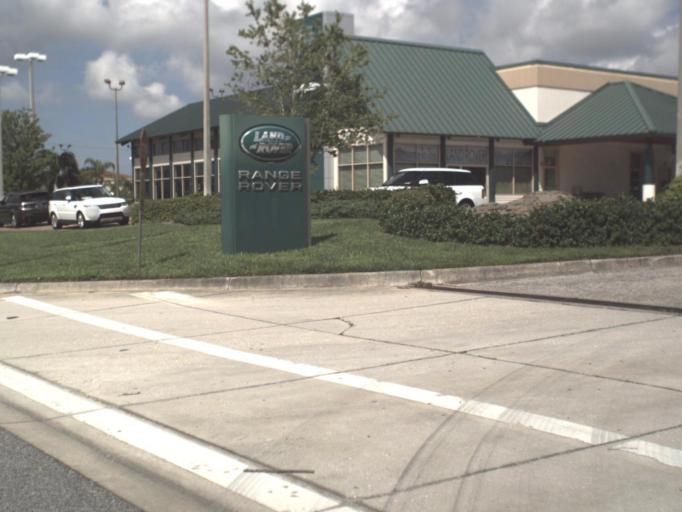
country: US
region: Florida
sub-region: Sarasota County
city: Bee Ridge
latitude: 27.2693
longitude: -82.4675
